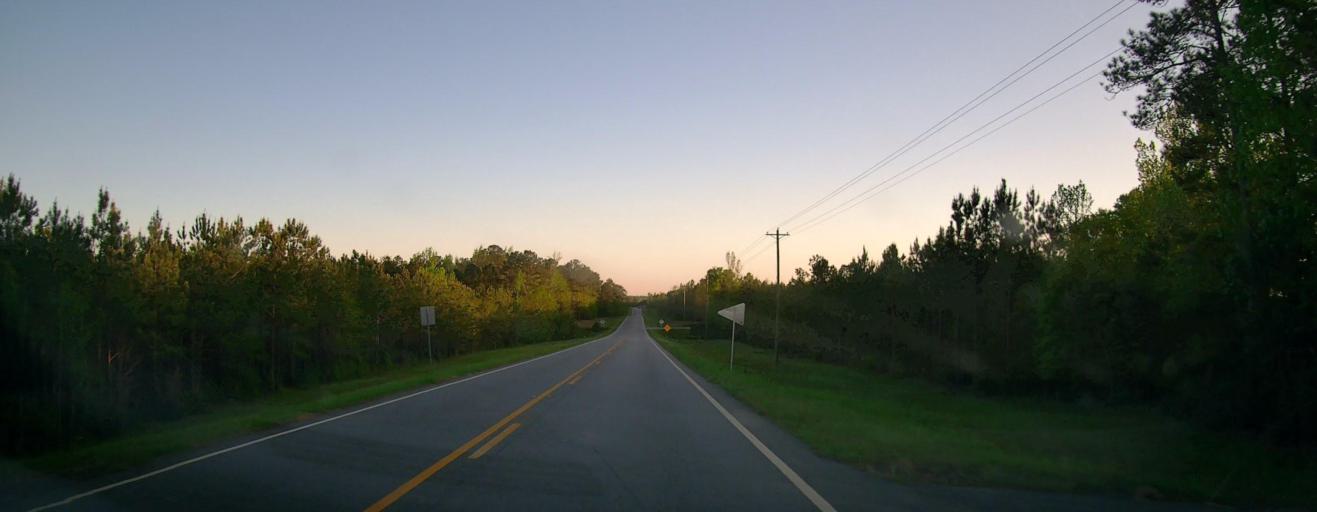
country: US
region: Georgia
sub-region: Talbot County
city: Talbotton
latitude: 32.5690
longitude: -84.5669
